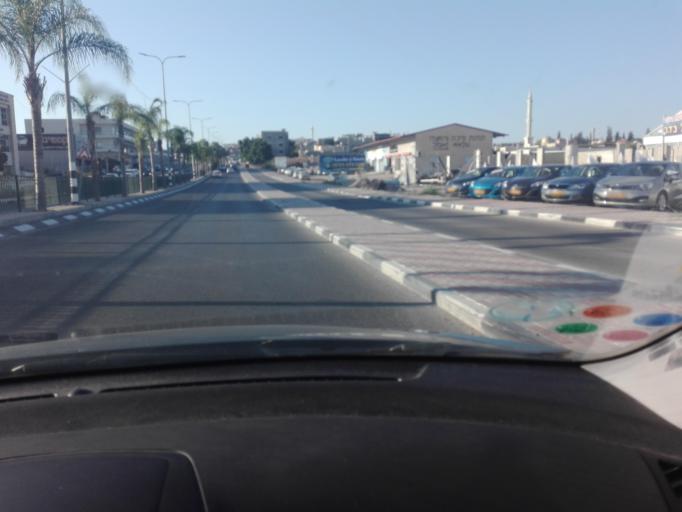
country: PS
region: West Bank
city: Nazlat `Isa
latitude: 32.4087
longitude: 35.0478
